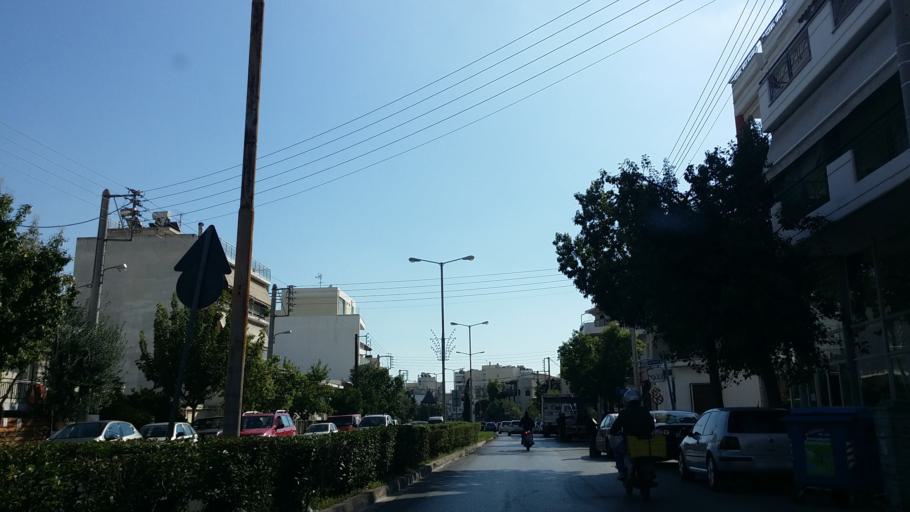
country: GR
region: Attica
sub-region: Nomarchia Athinas
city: Ilion
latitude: 38.0206
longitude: 23.7084
